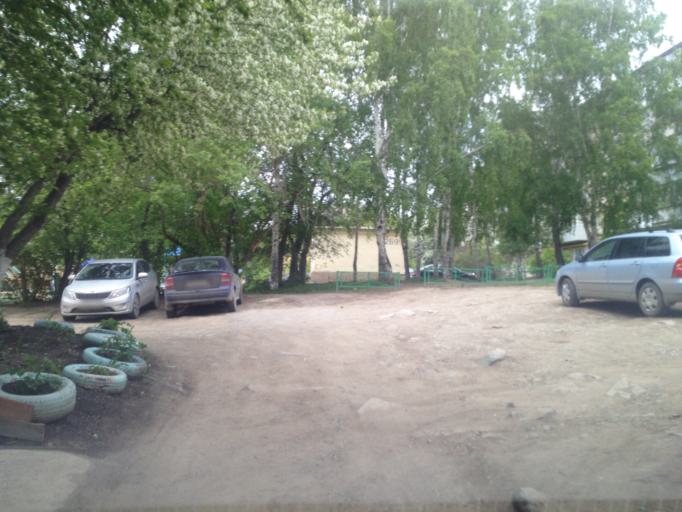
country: RU
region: Sverdlovsk
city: Sovkhoznyy
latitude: 56.7631
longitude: 60.6037
